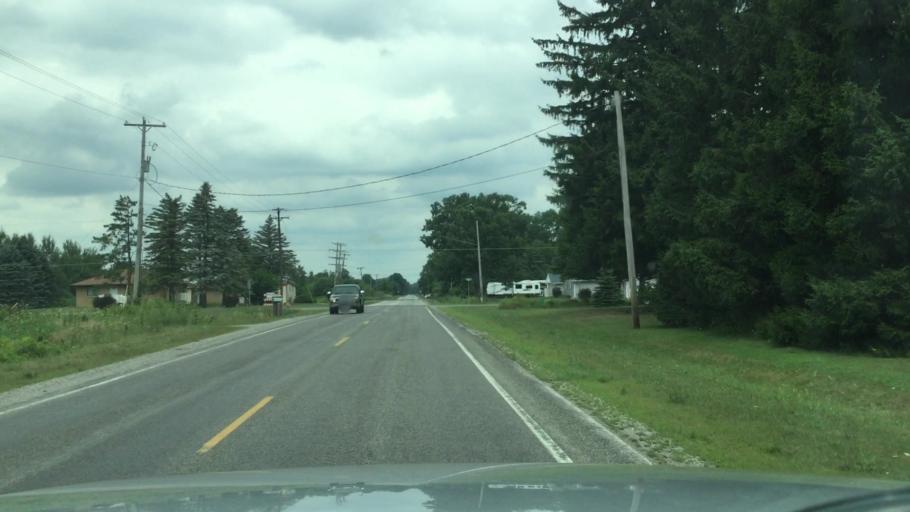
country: US
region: Michigan
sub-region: Saginaw County
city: Burt
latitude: 43.2939
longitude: -83.8944
